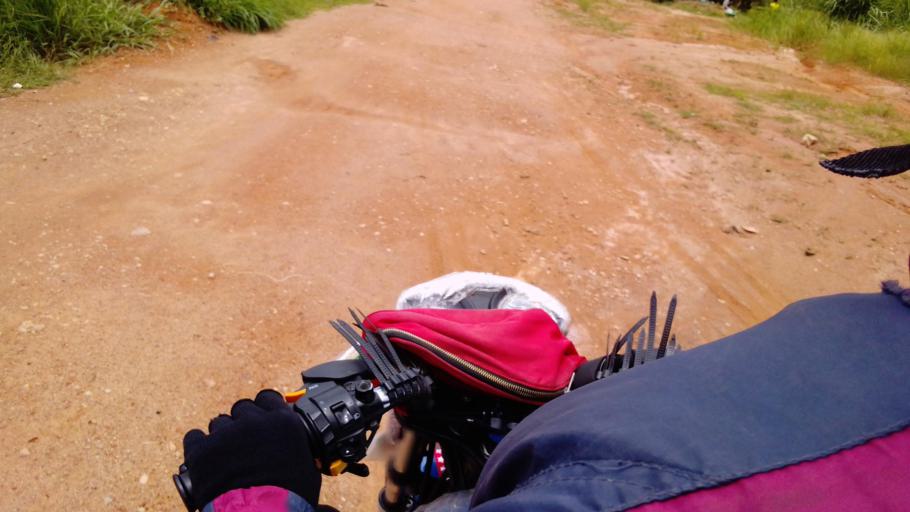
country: SL
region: Eastern Province
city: Koidu
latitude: 8.6788
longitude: -10.9552
